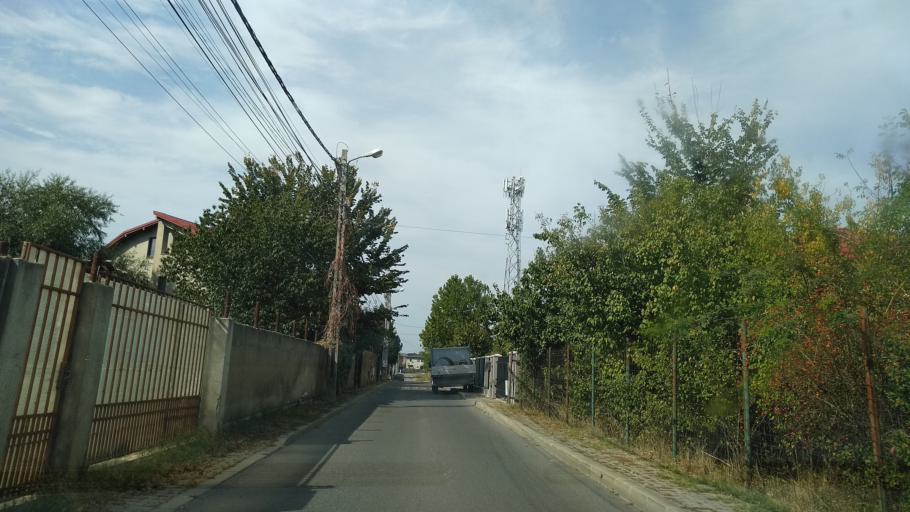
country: RO
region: Ilfov
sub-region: Comuna Chitila
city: Chitila
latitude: 44.5138
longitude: 25.9904
